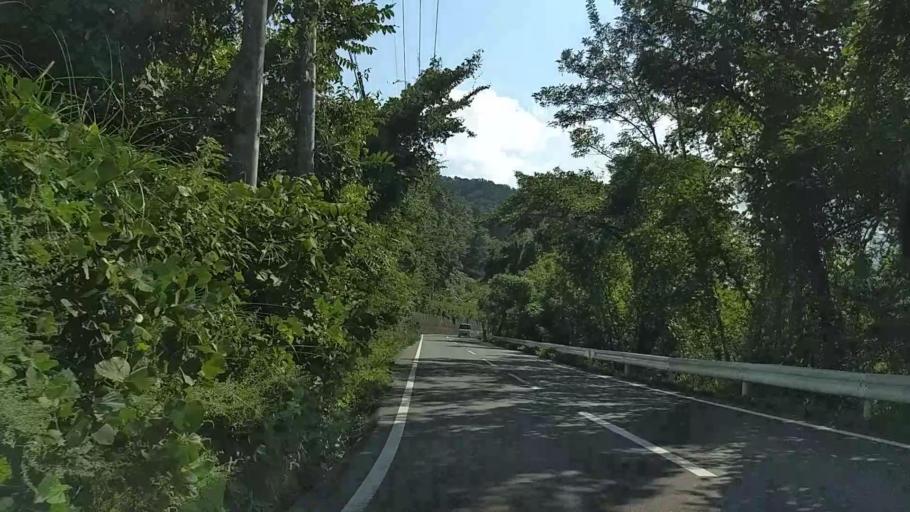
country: JP
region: Yamanashi
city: Fujikawaguchiko
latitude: 35.4067
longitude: 138.4557
